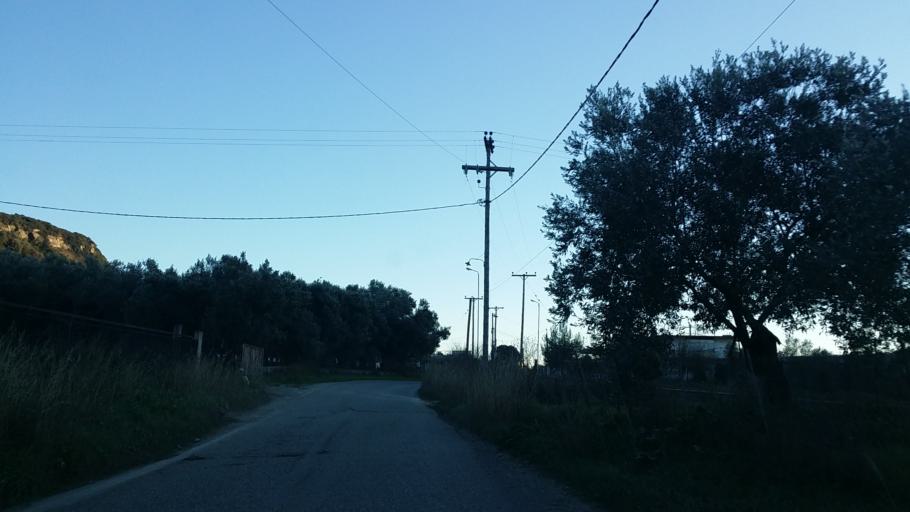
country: GR
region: West Greece
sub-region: Nomos Aitolias kai Akarnanias
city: Neapolis
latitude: 38.6997
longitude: 21.3529
